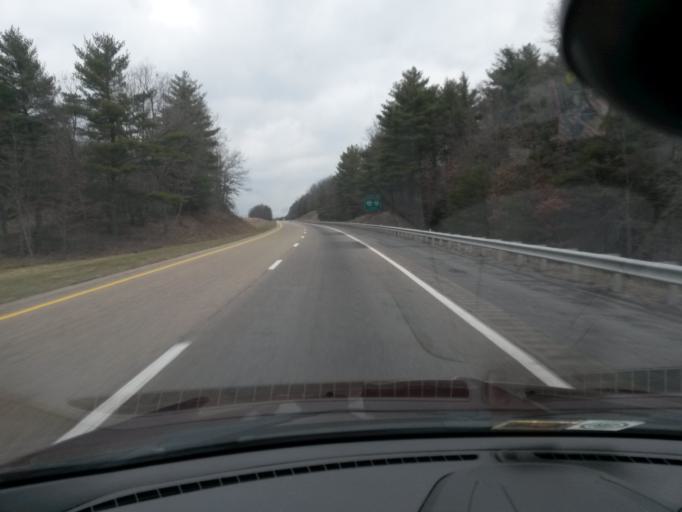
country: US
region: Virginia
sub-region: Alleghany County
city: Clifton Forge
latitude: 37.8207
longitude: -79.7433
